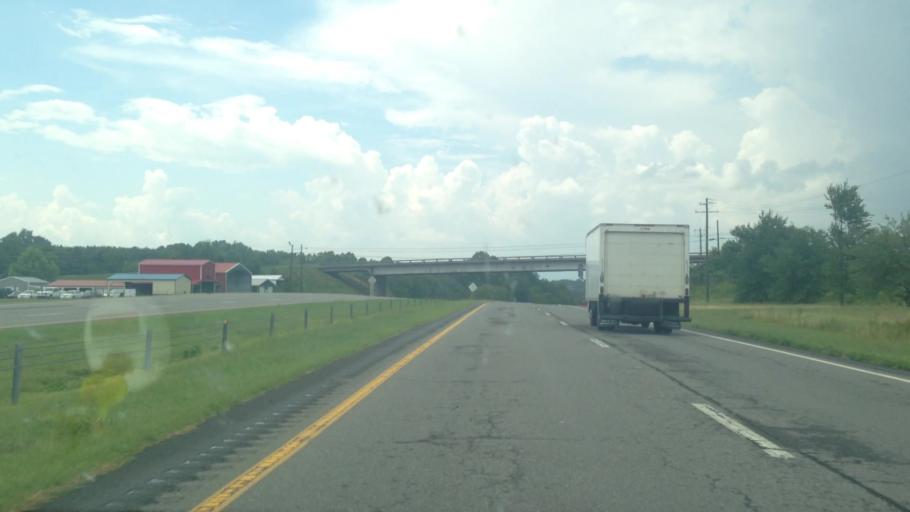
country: US
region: North Carolina
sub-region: Surry County
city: Flat Rock
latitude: 36.4590
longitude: -80.5600
